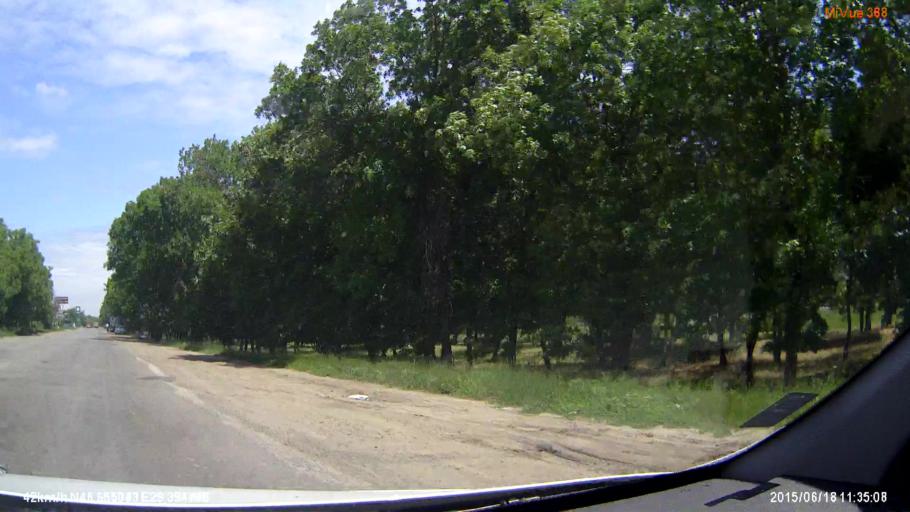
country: MD
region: Causeni
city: Causeni
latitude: 46.6559
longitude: 29.3940
